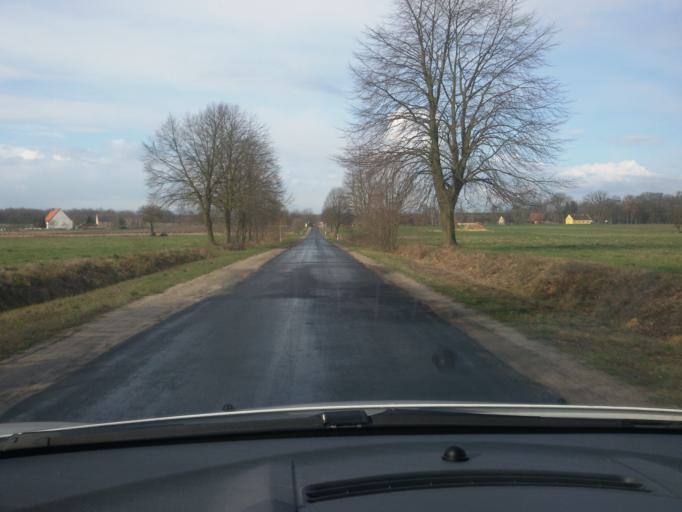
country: PL
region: Lubusz
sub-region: Powiat nowosolski
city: Nowe Miasteczko
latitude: 51.7154
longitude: 15.7652
